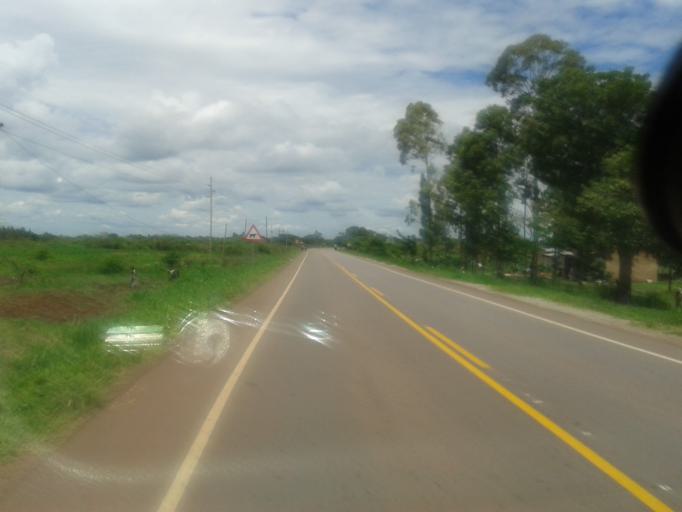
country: UG
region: Western Region
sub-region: Kiryandongo District
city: Kiryandongo
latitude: 1.7867
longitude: 32.0158
